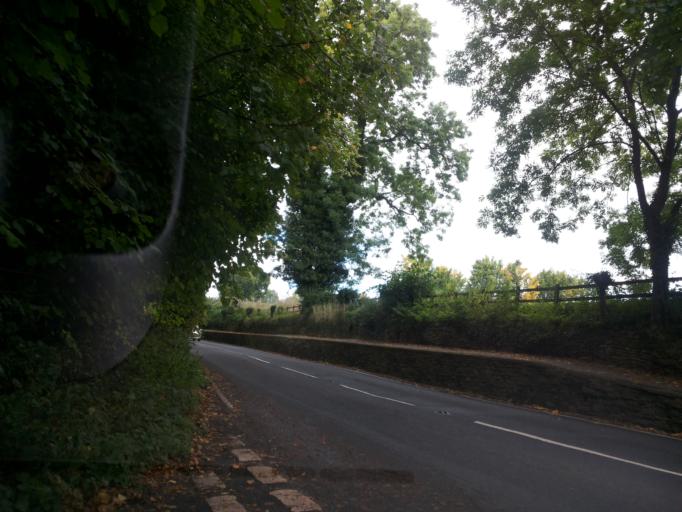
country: GB
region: England
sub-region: North Yorkshire
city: Catterick Garrison
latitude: 54.4035
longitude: -1.7199
